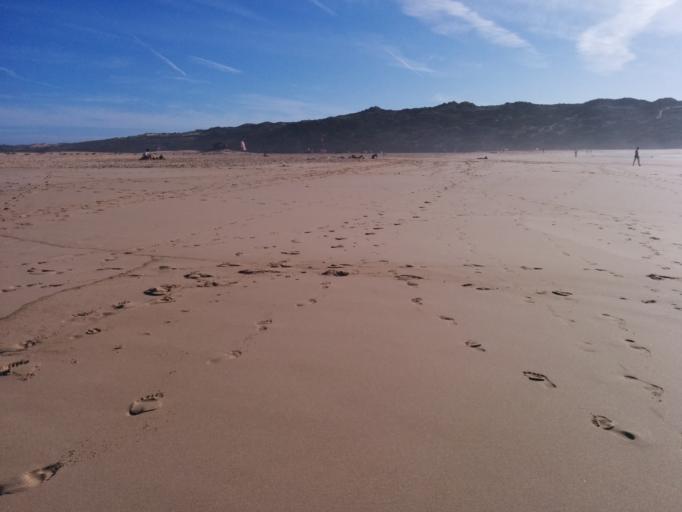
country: PT
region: Faro
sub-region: Vila do Bispo
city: Vila do Bispo
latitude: 37.1997
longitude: -8.9021
